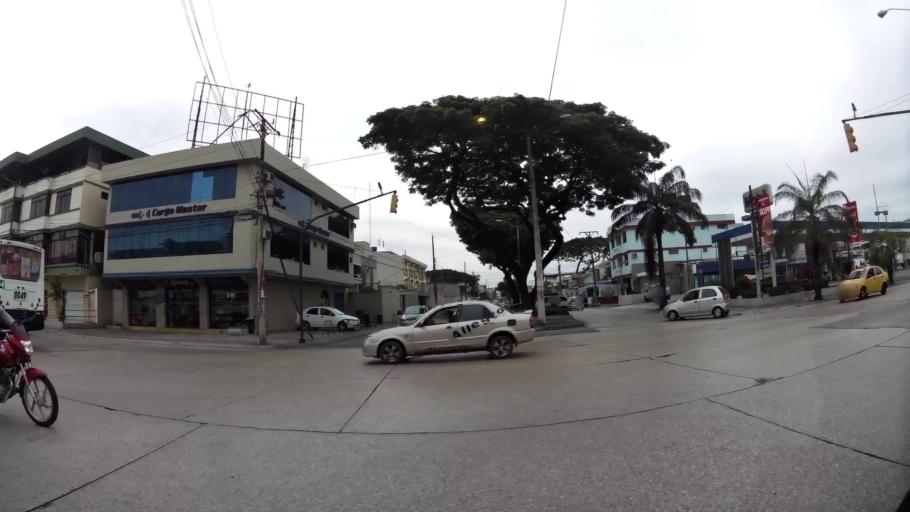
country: EC
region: Guayas
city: Eloy Alfaro
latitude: -2.1479
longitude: -79.8930
